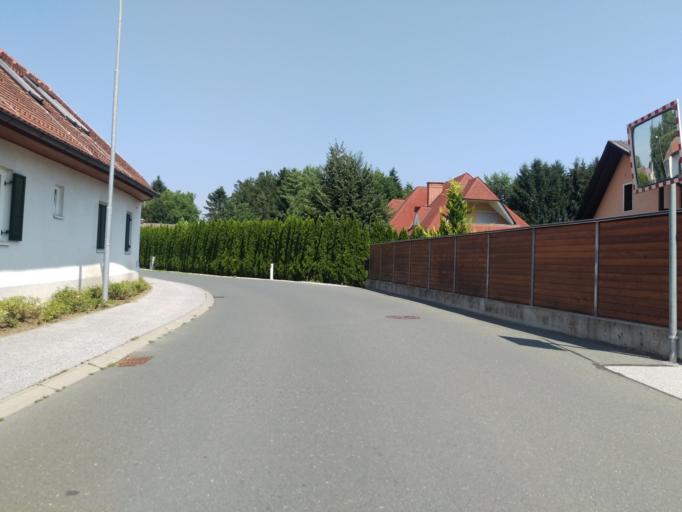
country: AT
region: Styria
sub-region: Politischer Bezirk Graz-Umgebung
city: Kalsdorf bei Graz
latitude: 46.9584
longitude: 15.4857
